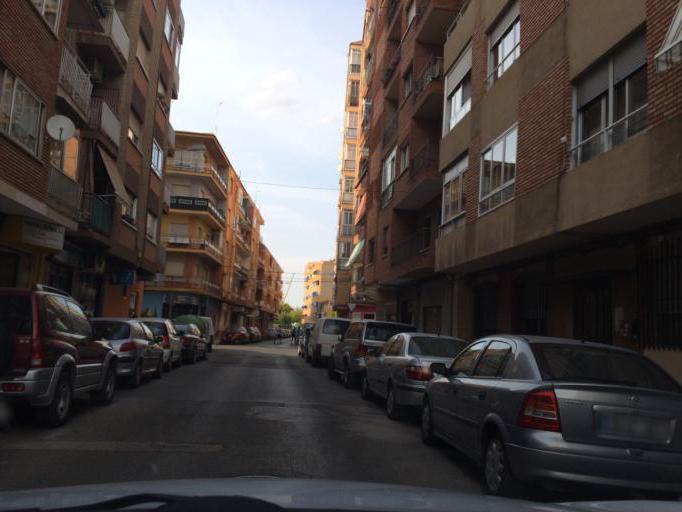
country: ES
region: Castille-La Mancha
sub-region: Provincia de Albacete
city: Albacete
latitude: 38.9942
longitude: -1.8687
